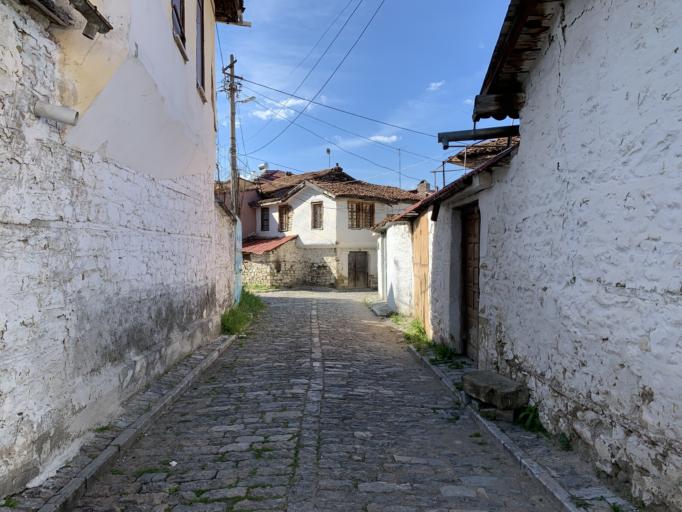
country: AL
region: Korce
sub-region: Rrethi i Korces
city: Korce
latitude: 40.6143
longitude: 20.7831
